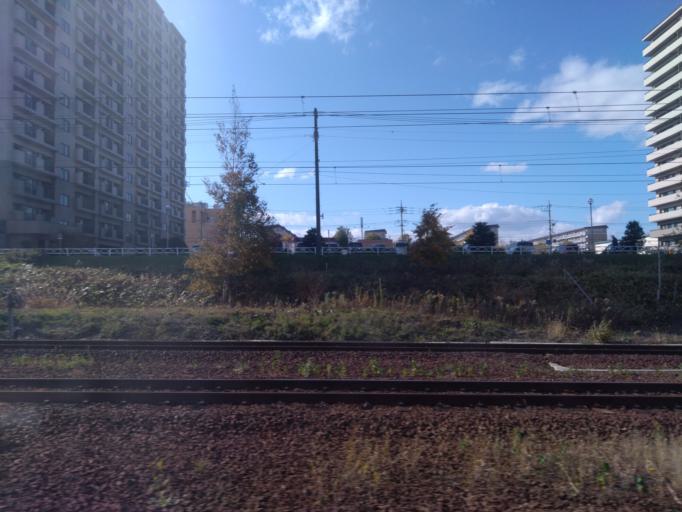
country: JP
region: Hokkaido
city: Kitahiroshima
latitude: 42.9809
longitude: 141.5630
